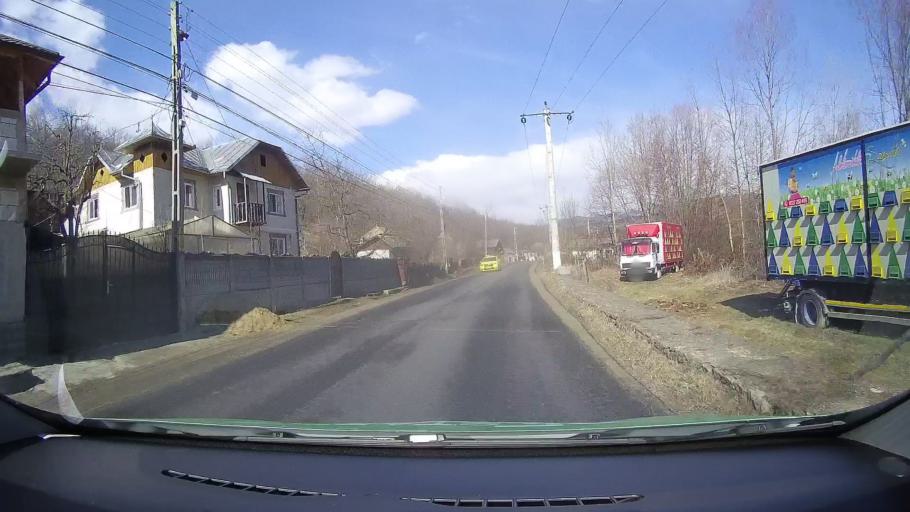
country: RO
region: Dambovita
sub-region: Comuna Runcu
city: Badeni
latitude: 45.1639
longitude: 25.3958
